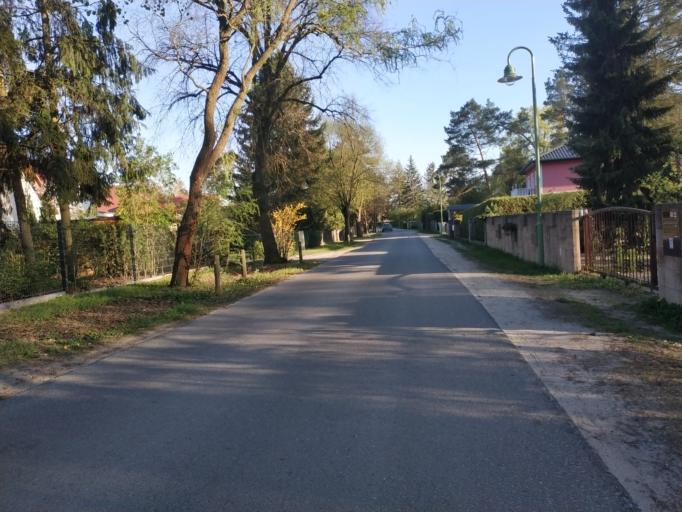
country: DE
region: Brandenburg
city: Petershagen
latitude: 52.5462
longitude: 13.8334
